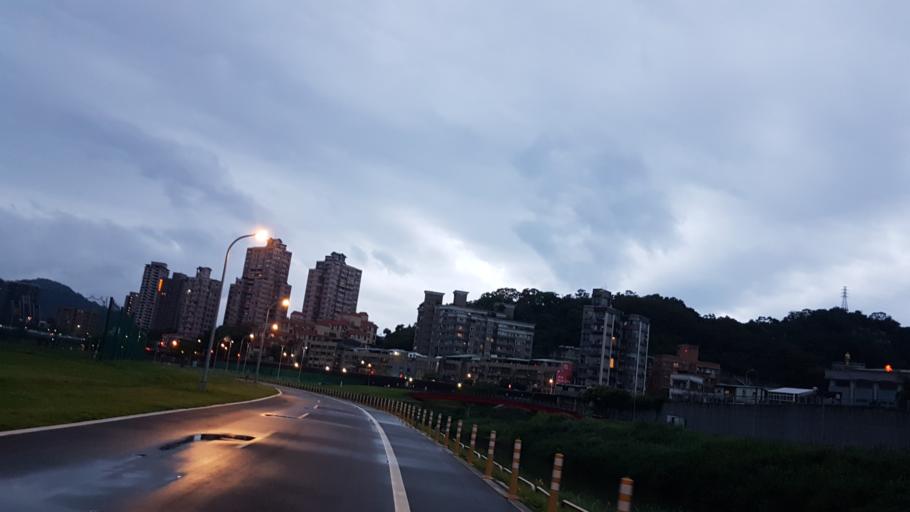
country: TW
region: Taipei
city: Taipei
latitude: 24.9957
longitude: 121.5736
